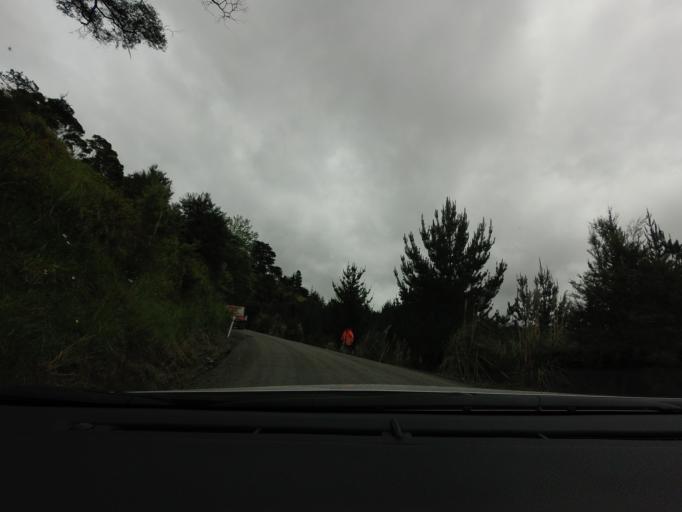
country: NZ
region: Auckland
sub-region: Auckland
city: Warkworth
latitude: -36.4881
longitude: 174.6165
